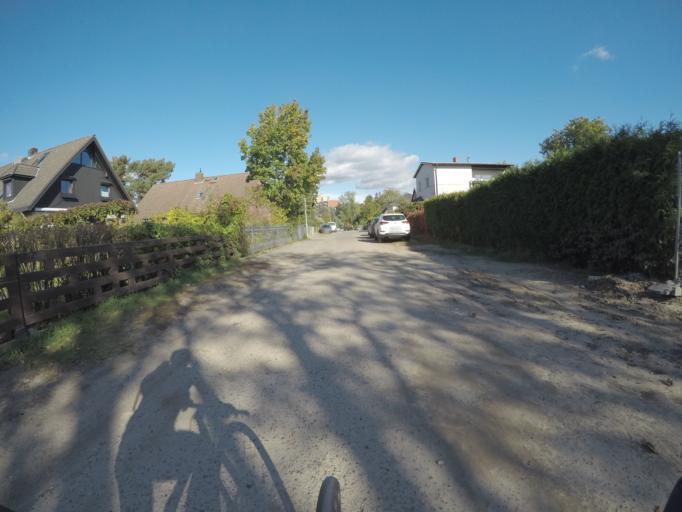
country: DE
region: Berlin
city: Staaken
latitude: 52.5276
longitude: 13.1546
